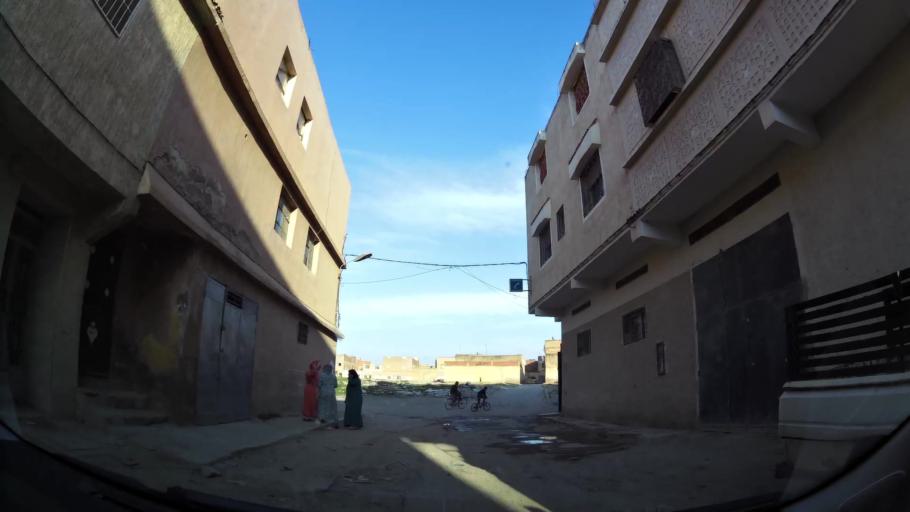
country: MA
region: Oriental
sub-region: Oujda-Angad
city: Oujda
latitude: 34.7041
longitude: -1.9097
